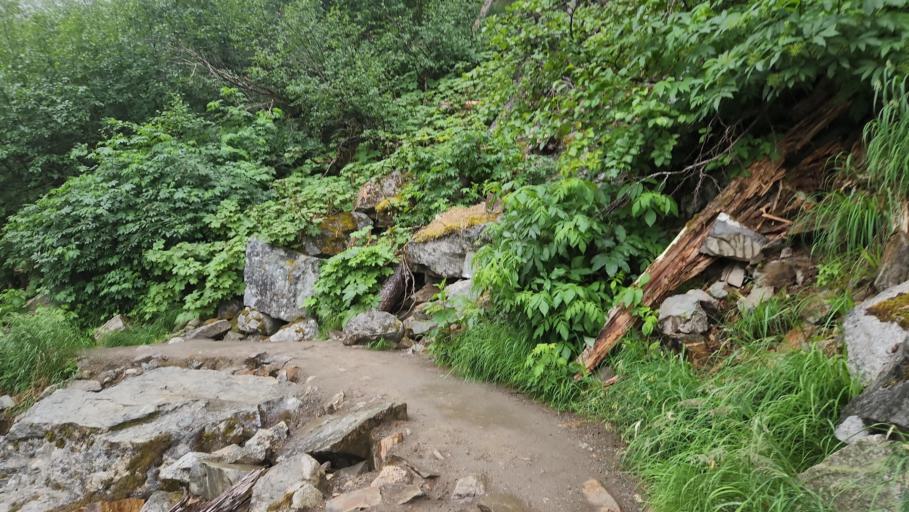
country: CA
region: British Columbia
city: Pemberton
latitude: 50.3599
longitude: -122.4907
